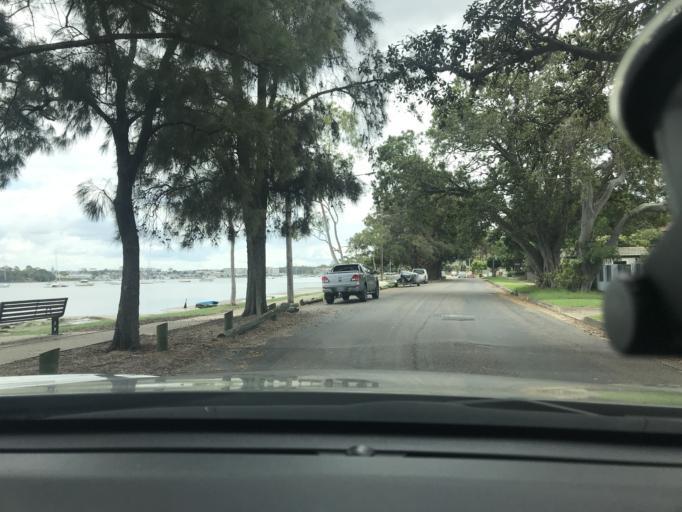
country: AU
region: New South Wales
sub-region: Canada Bay
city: Wareemba
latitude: -33.8582
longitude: 151.1282
